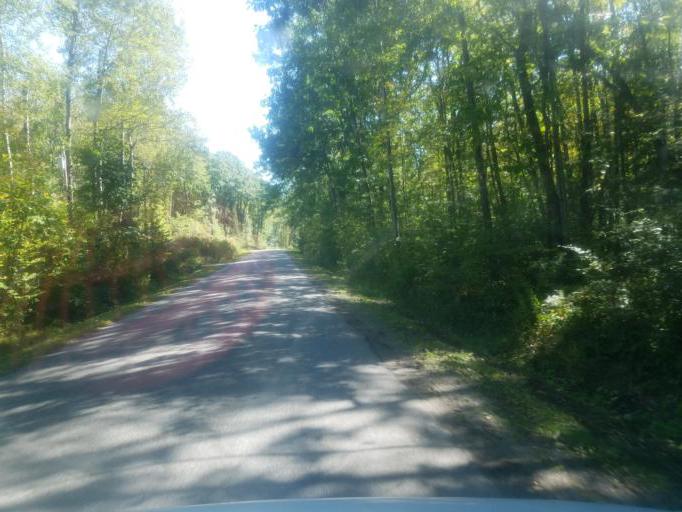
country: US
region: New York
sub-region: Allegany County
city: Cuba
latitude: 42.3102
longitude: -78.2038
